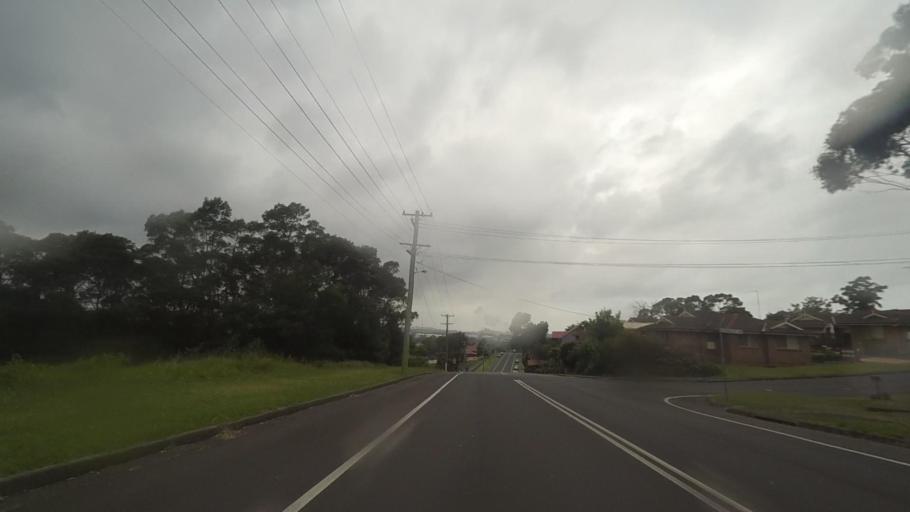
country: AU
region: New South Wales
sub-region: Wollongong
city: Cordeaux Heights
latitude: -34.4577
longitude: 150.8286
